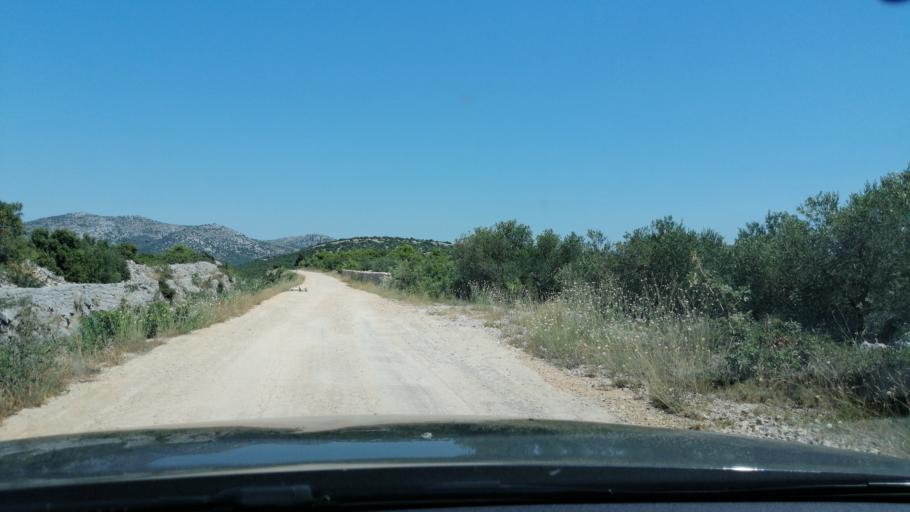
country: HR
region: Sibensko-Kniniska
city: Murter
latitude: 43.8462
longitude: 15.6263
